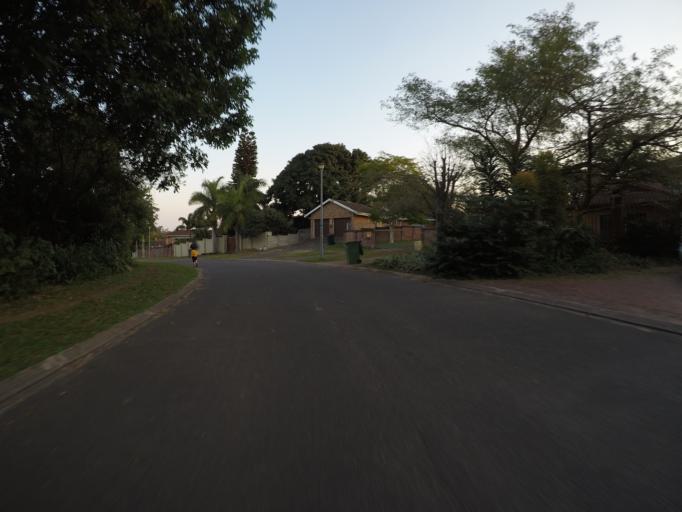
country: ZA
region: KwaZulu-Natal
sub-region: uThungulu District Municipality
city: Richards Bay
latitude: -28.7675
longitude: 32.1228
